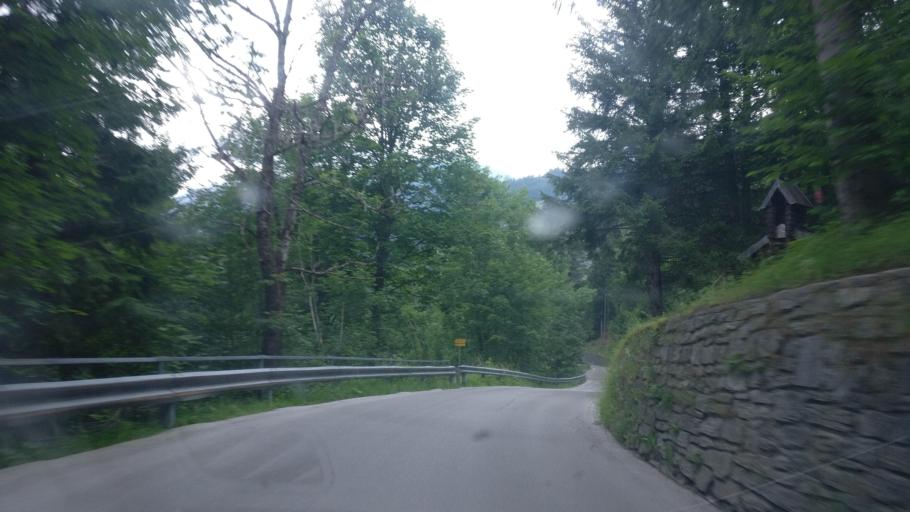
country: AT
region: Salzburg
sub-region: Politischer Bezirk Sankt Johann im Pongau
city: Bad Gastein
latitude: 47.1210
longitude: 13.1447
